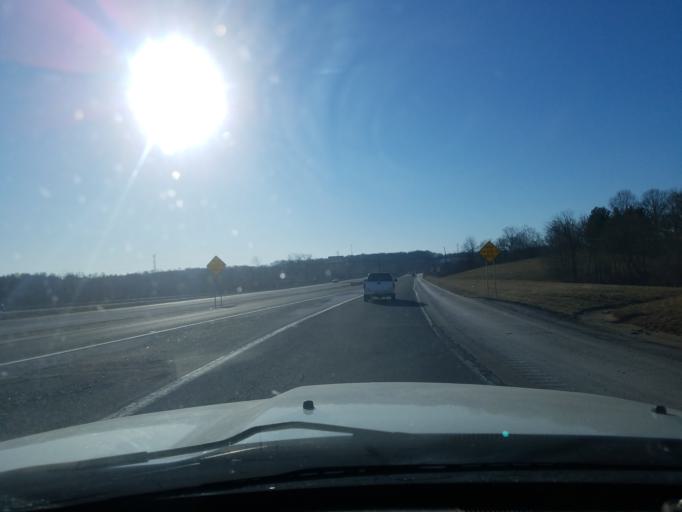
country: US
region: Indiana
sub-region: Lawrence County
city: Bedford
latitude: 38.8280
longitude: -86.5082
